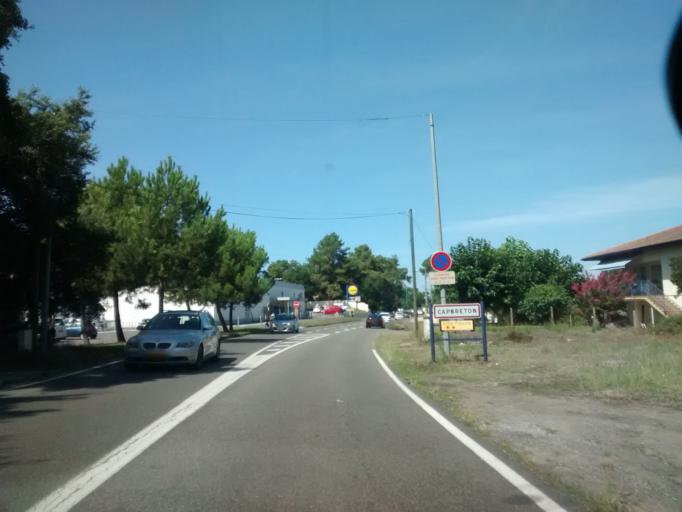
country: FR
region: Aquitaine
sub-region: Departement des Landes
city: Capbreton
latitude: 43.6363
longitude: -1.4187
